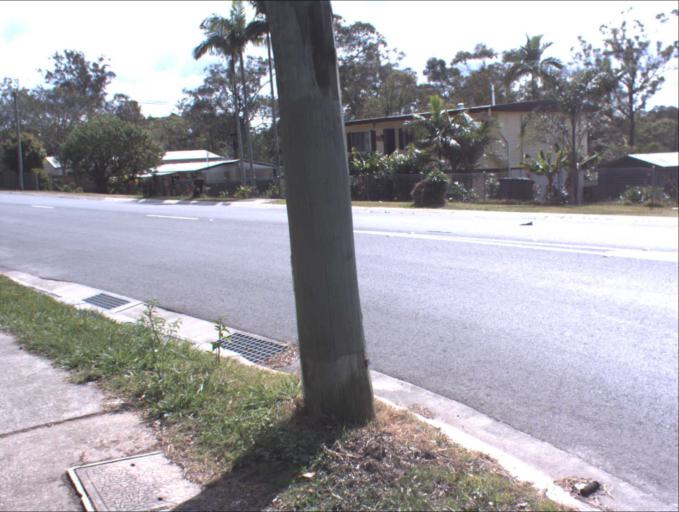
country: AU
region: Queensland
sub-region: Logan
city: Logan City
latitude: -27.6525
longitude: 153.1232
